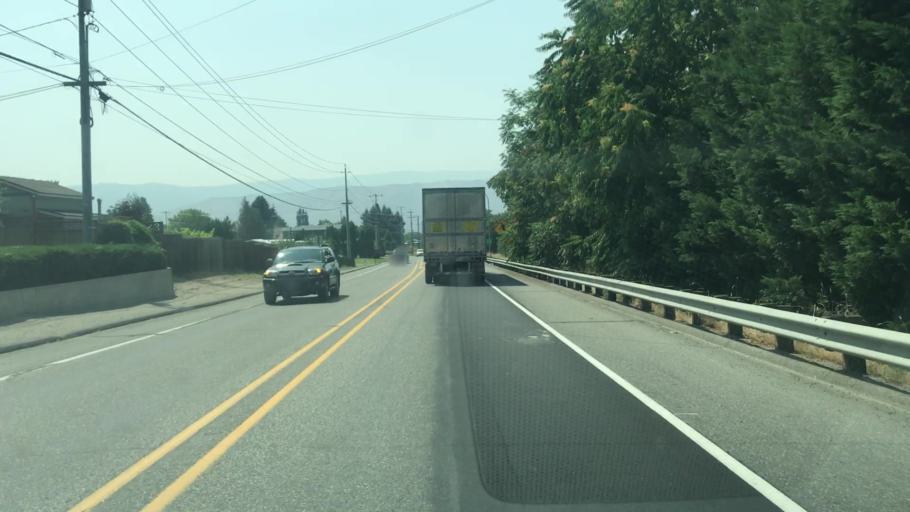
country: US
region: Washington
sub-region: Chelan County
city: Wenatchee
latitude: 47.4445
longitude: -120.2974
